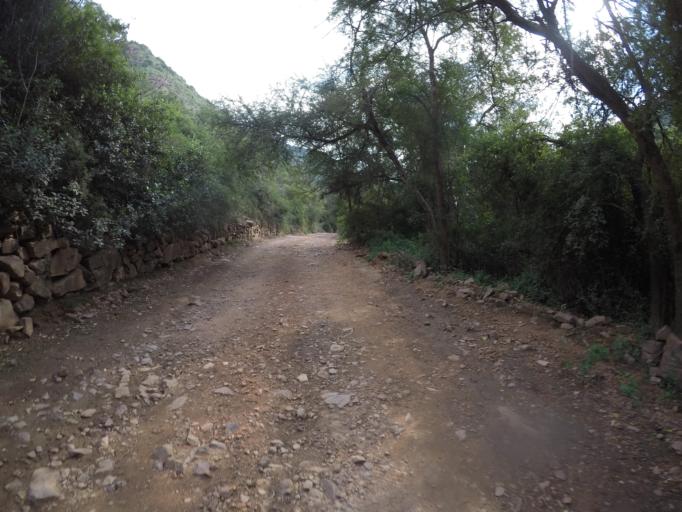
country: ZA
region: Eastern Cape
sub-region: Cacadu District Municipality
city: Kareedouw
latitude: -33.6420
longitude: 24.3126
